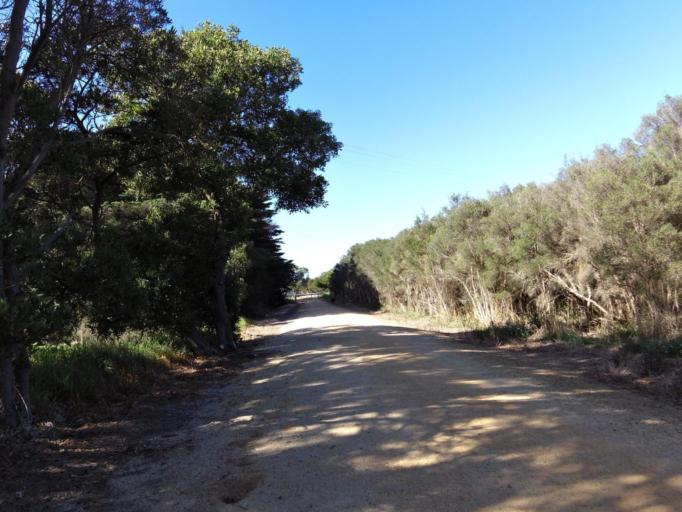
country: AU
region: Victoria
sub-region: Bass Coast
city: North Wonthaggi
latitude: -38.5876
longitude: 145.5572
